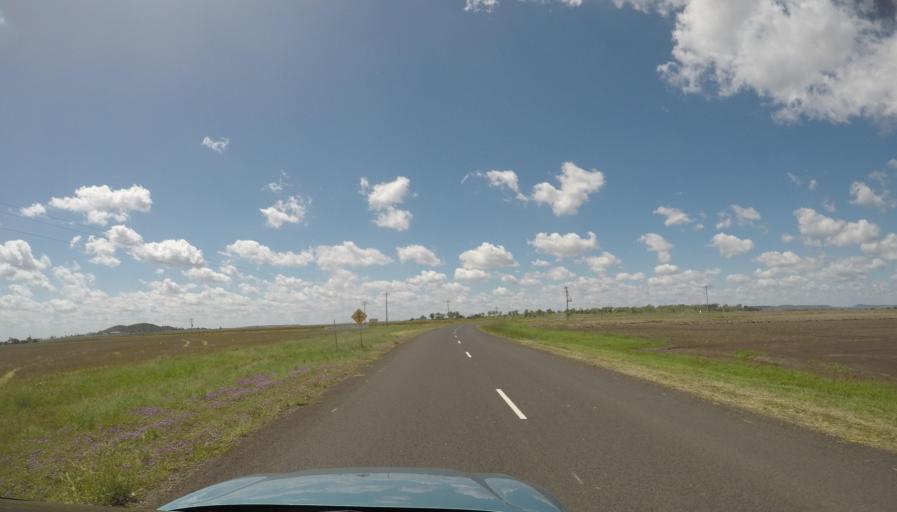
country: AU
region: Queensland
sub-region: Toowoomba
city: Oakey
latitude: -27.5274
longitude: 151.5759
